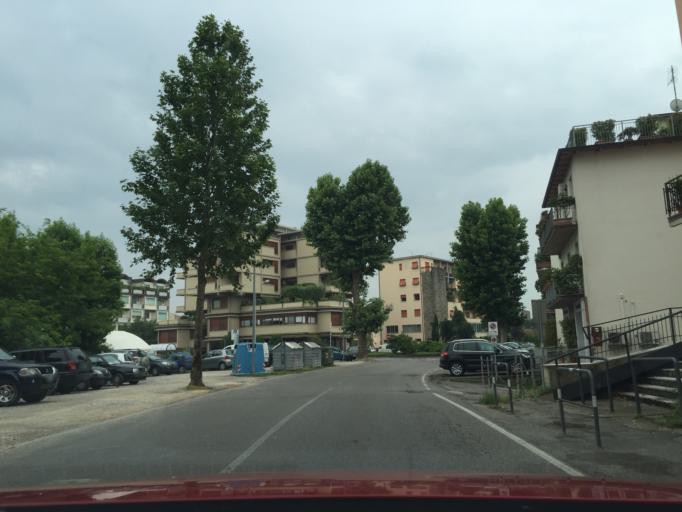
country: IT
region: Tuscany
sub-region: Provincia di Pistoia
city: Pistoia
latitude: 43.9408
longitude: 10.9124
